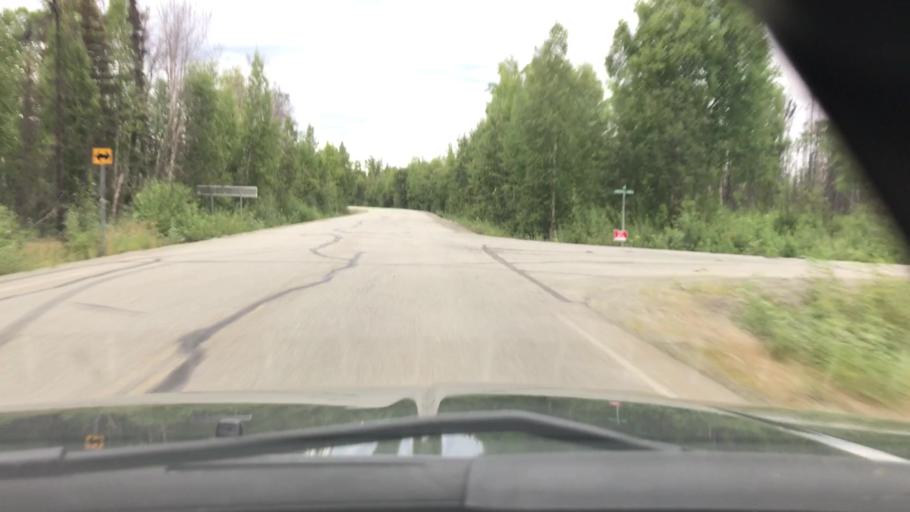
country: US
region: Alaska
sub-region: Matanuska-Susitna Borough
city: Willow
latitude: 61.7603
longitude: -150.1212
